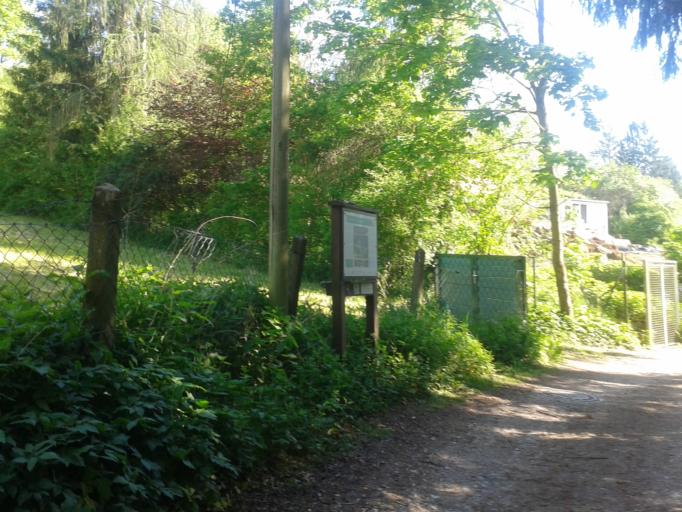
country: DE
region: Bavaria
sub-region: Upper Franconia
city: Bamberg
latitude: 49.8865
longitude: 10.8720
